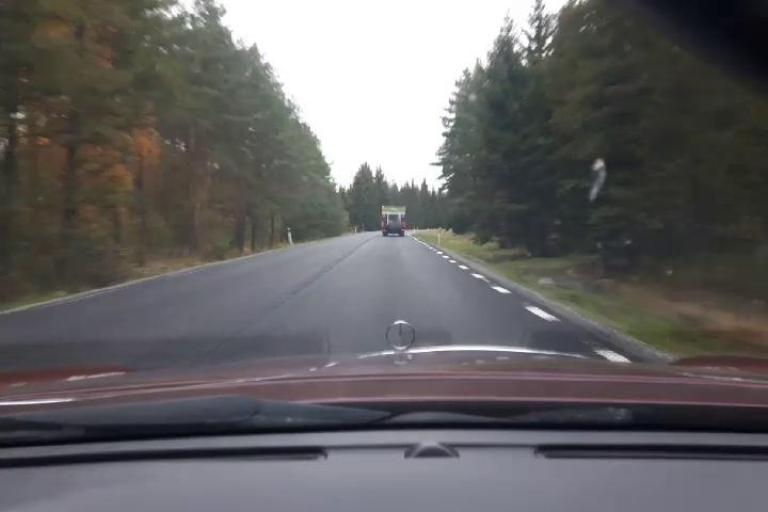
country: SE
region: Soedermanland
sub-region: Strangnas Kommun
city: Strangnas
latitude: 59.4162
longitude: 17.0195
